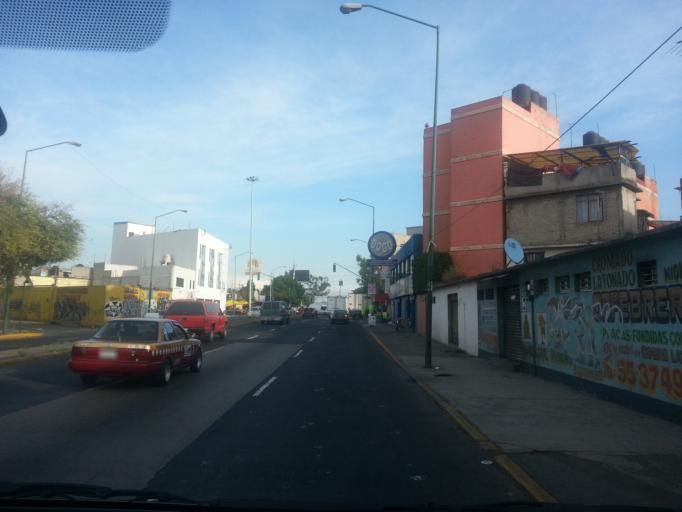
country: MX
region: Mexico City
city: Cuauhtemoc
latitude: 19.4654
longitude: -99.1333
